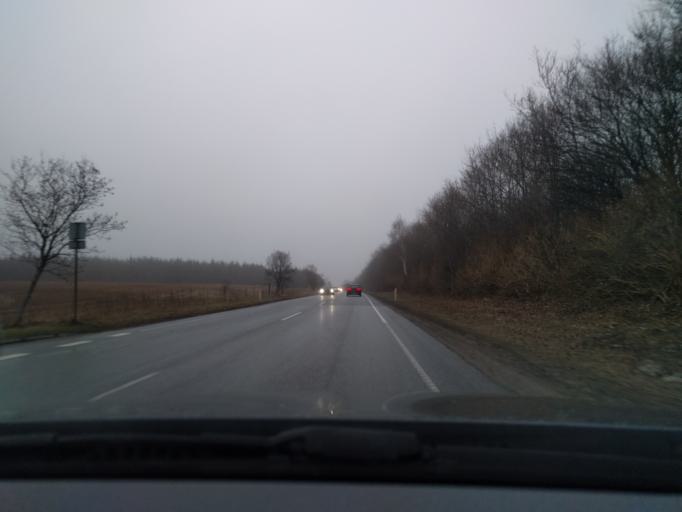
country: DK
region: Central Jutland
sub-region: Viborg Kommune
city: Viborg
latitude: 56.4696
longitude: 9.4622
